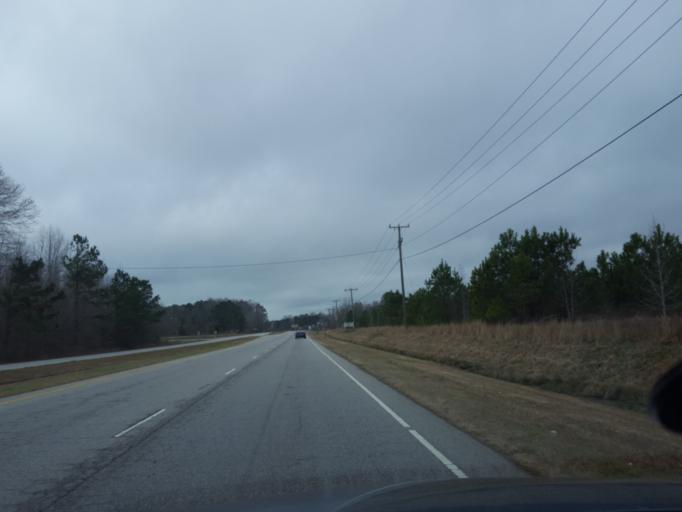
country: US
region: North Carolina
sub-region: Washington County
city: Plymouth
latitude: 35.8092
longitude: -76.8788
